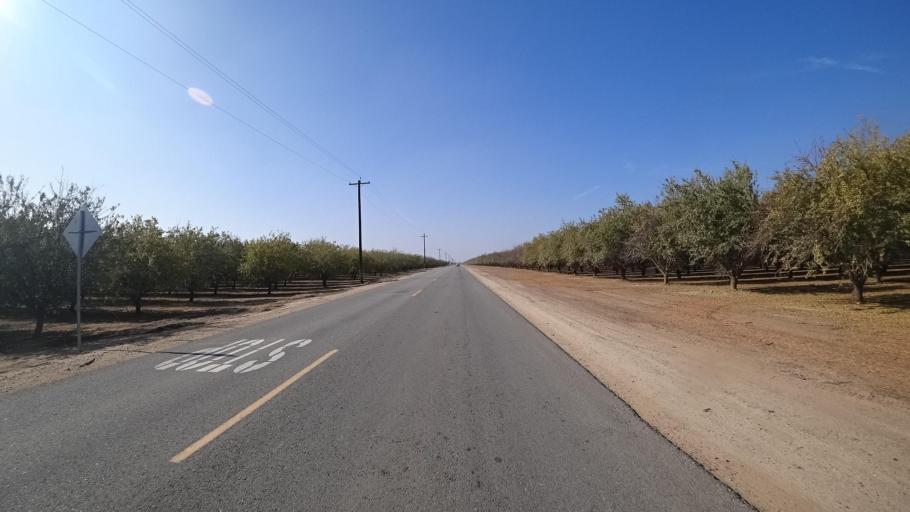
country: US
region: California
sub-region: Kern County
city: Shafter
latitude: 35.5297
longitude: -119.1536
